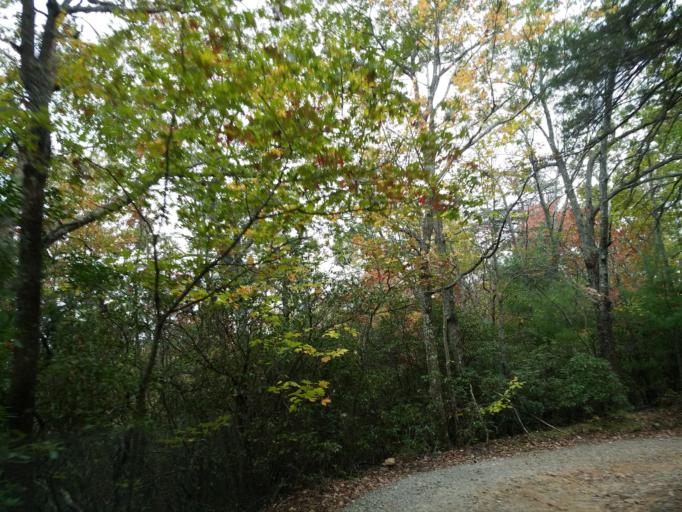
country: US
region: Georgia
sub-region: Dawson County
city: Dawsonville
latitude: 34.5857
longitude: -84.2333
